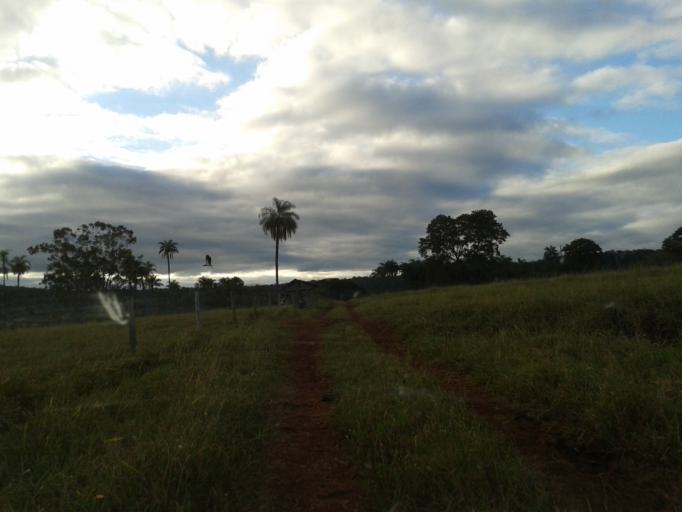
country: BR
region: Minas Gerais
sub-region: Campina Verde
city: Campina Verde
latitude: -19.4648
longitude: -49.6524
